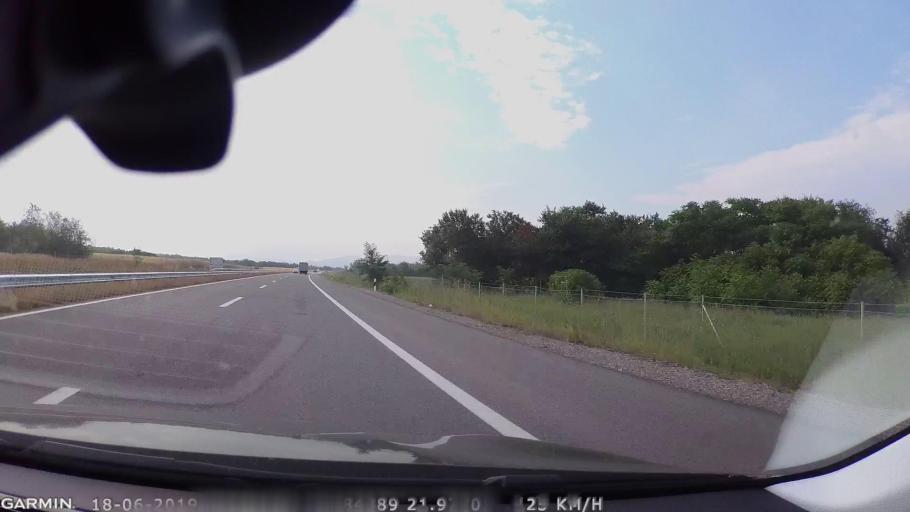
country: MK
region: Sveti Nikole
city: Sveti Nikole
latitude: 41.8481
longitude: 21.9695
